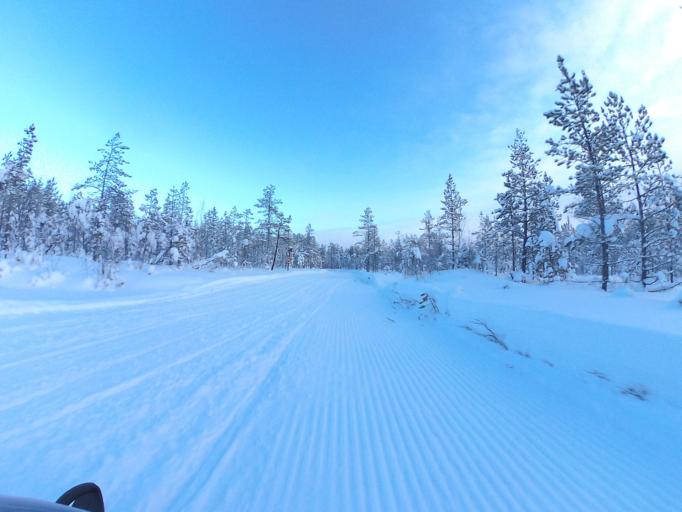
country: FI
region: Lapland
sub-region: Rovaniemi
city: Rovaniemi
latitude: 66.5130
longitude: 25.9683
